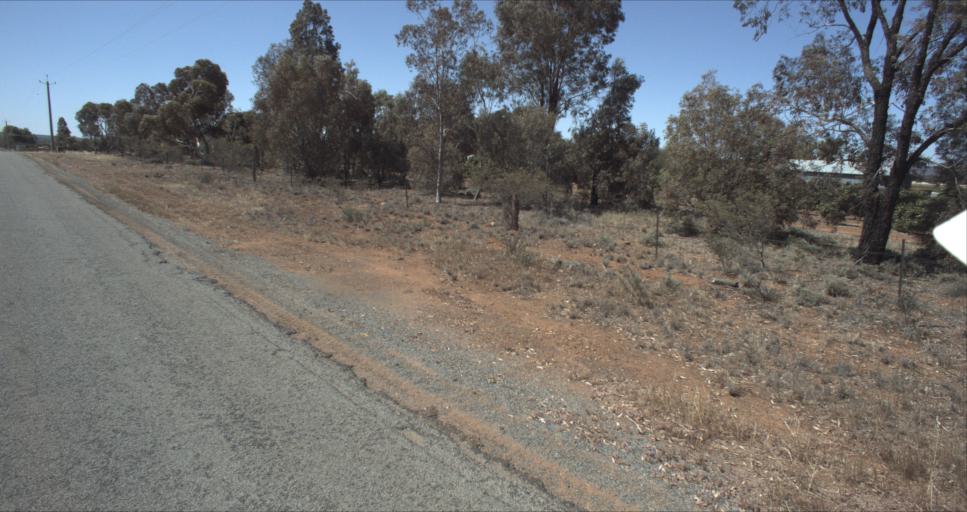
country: AU
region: New South Wales
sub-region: Leeton
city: Leeton
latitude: -34.4843
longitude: 146.4145
